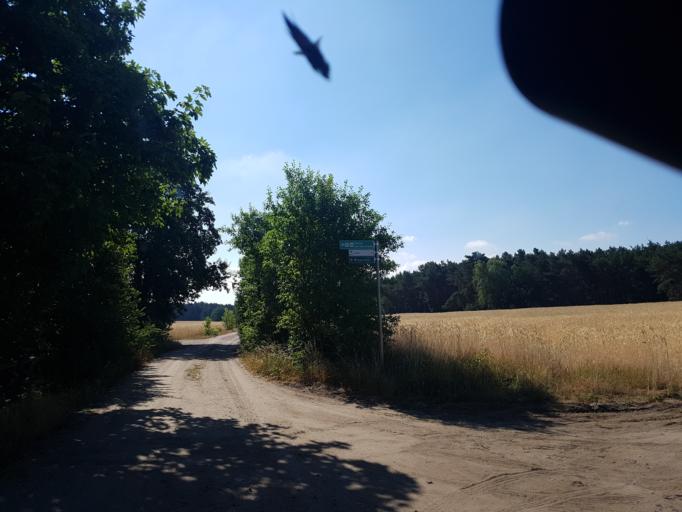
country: DE
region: Brandenburg
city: Treuenbrietzen
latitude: 52.0377
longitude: 12.8695
